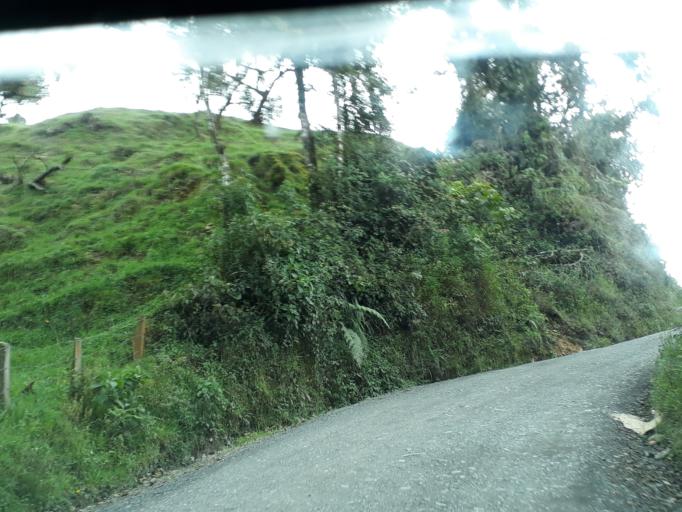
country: CO
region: Cundinamarca
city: Pacho
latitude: 5.2485
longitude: -74.1820
